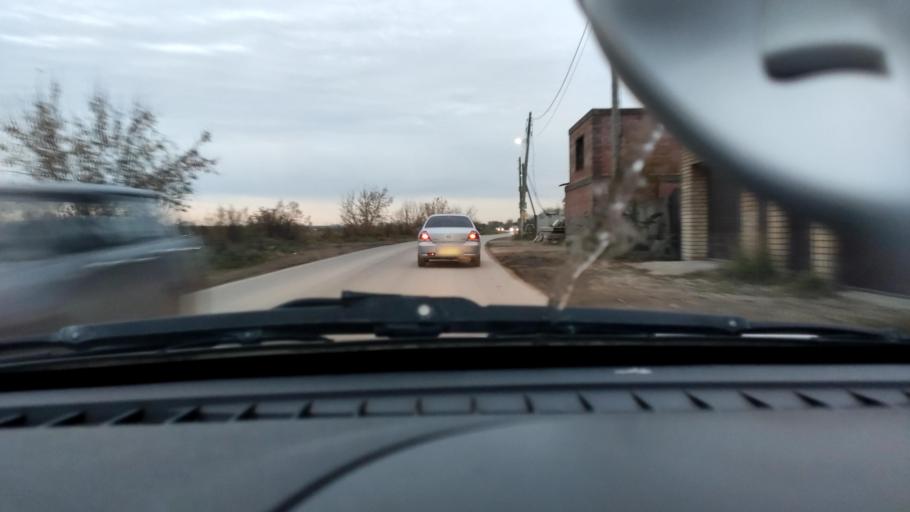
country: RU
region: Perm
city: Kondratovo
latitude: 57.9879
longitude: 56.0976
